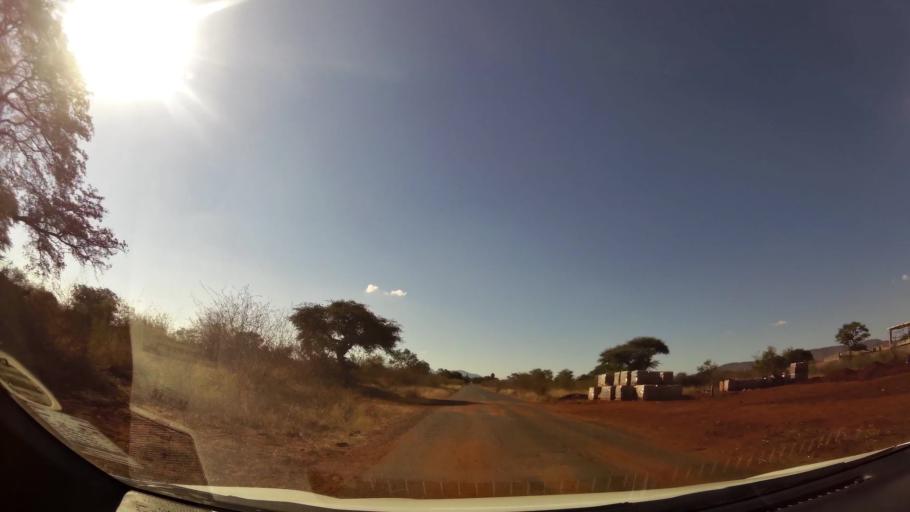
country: ZA
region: Limpopo
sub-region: Waterberg District Municipality
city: Mokopane
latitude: -24.2043
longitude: 28.9919
